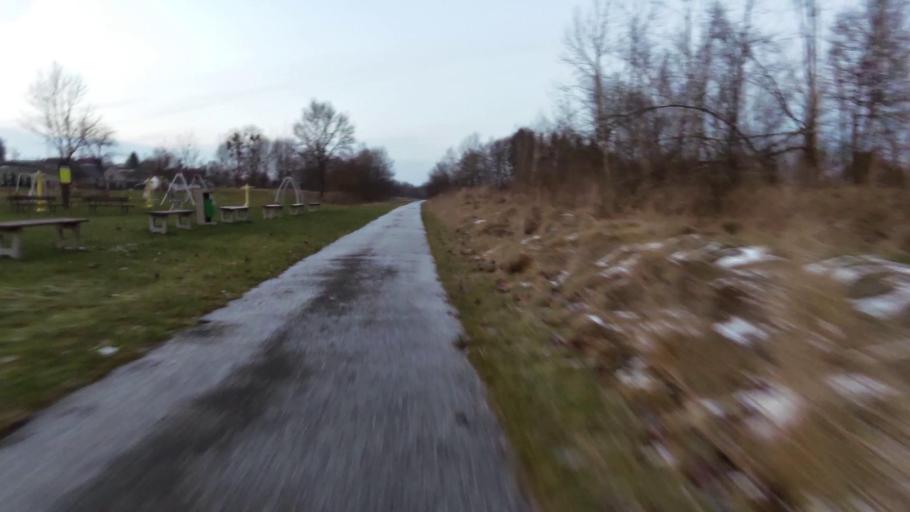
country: PL
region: West Pomeranian Voivodeship
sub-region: Powiat swidwinski
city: Polczyn-Zdroj
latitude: 53.7314
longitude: 16.0432
